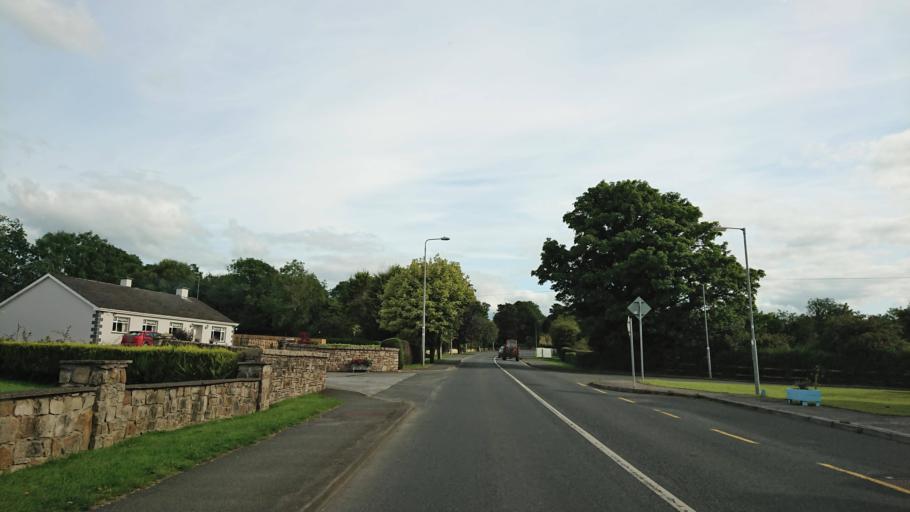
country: IE
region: Connaught
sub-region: County Leitrim
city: Carrick-on-Shannon
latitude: 53.9888
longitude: -8.0640
